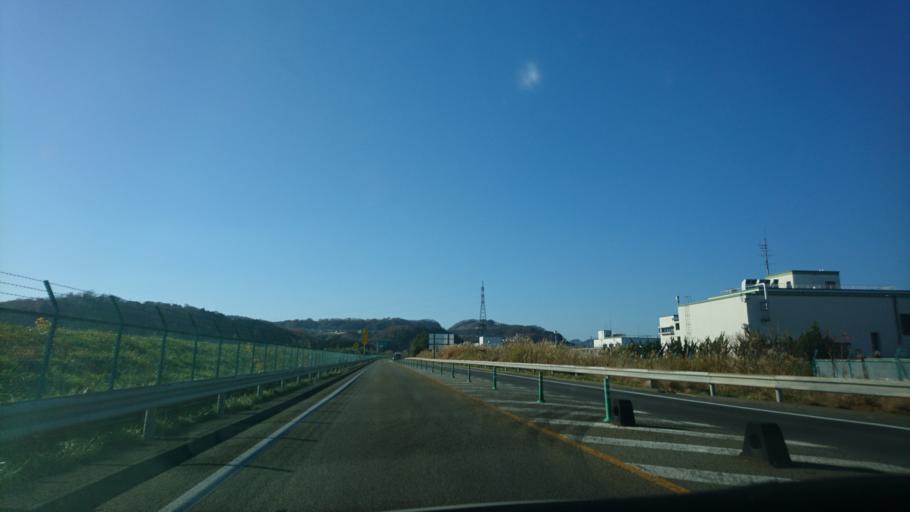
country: JP
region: Miyagi
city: Sendai
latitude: 38.2065
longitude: 140.8552
